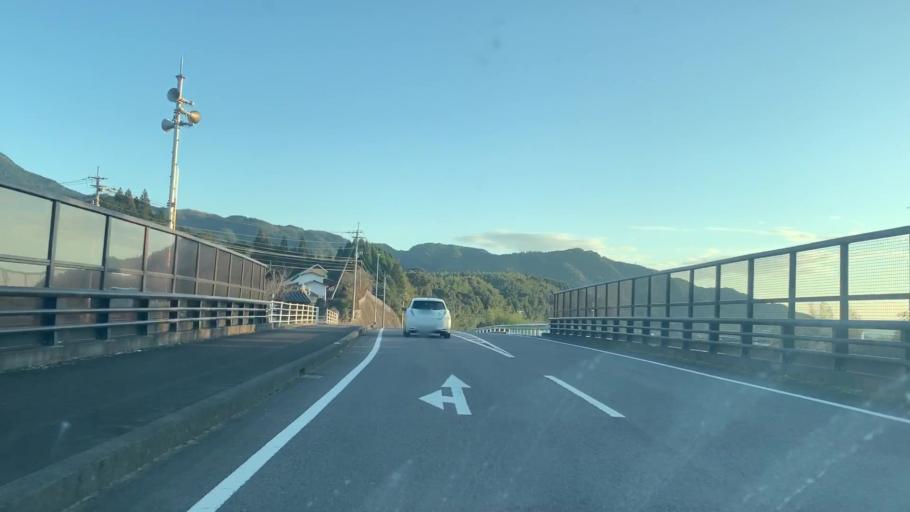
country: JP
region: Saga Prefecture
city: Imaricho-ko
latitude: 33.2920
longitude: 129.9702
